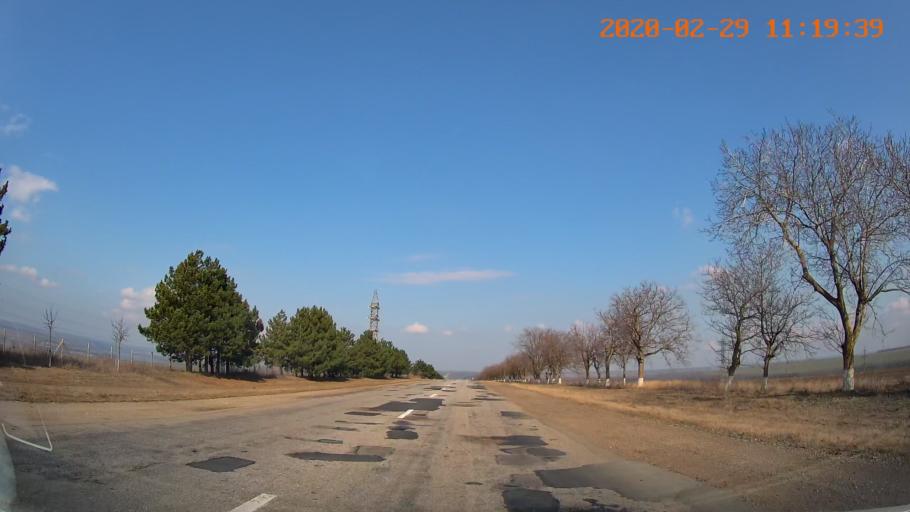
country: MD
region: Telenesti
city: Cocieri
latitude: 47.3532
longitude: 29.1739
